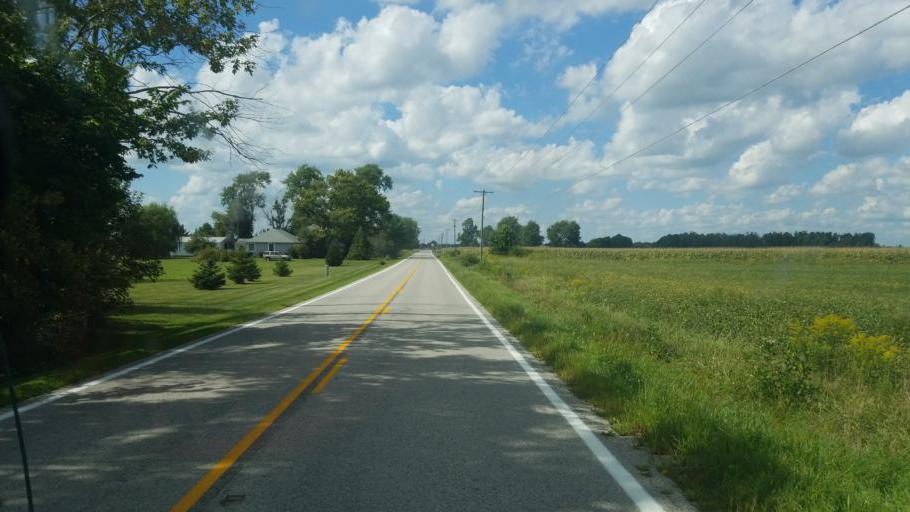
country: US
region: Ohio
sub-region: Union County
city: Richwood
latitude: 40.3723
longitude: -83.2692
